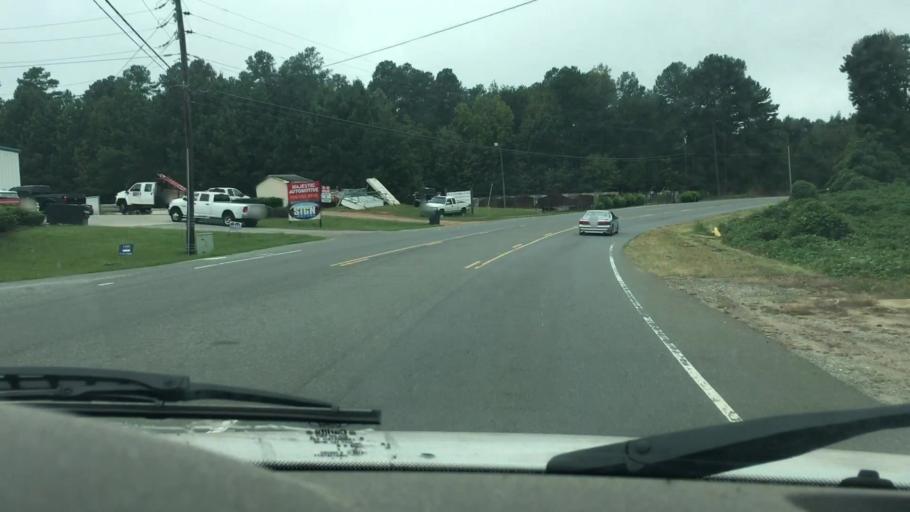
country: US
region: North Carolina
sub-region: Catawba County
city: Lake Norman of Catawba
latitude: 35.6014
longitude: -80.9168
